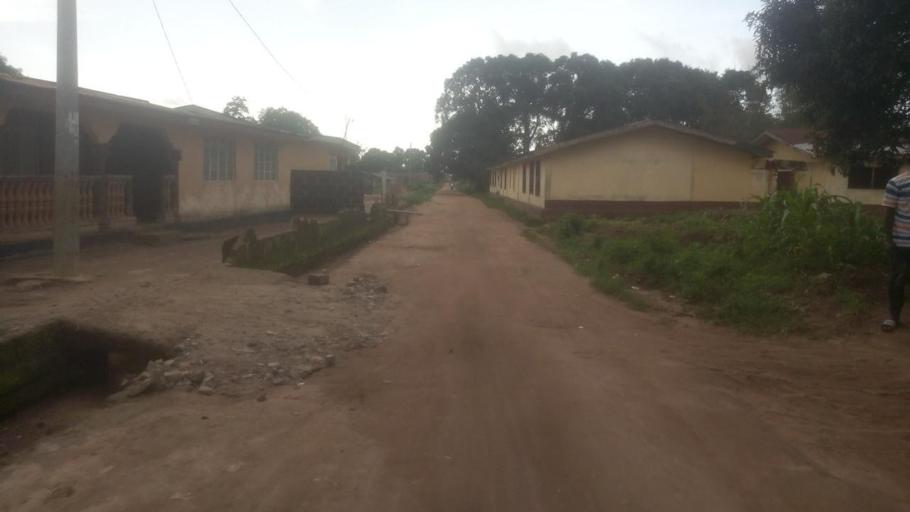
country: SL
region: Northern Province
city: Masoyila
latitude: 8.6072
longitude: -13.1875
